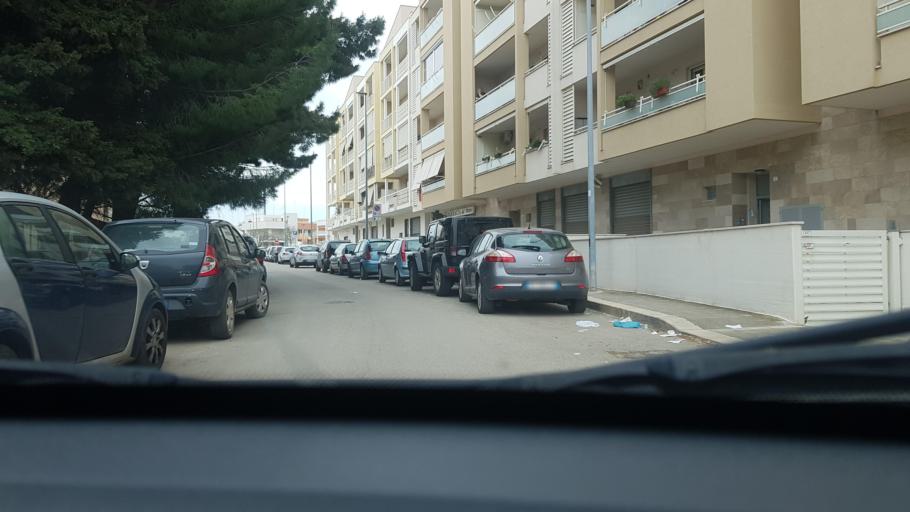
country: IT
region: Apulia
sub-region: Provincia di Bari
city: Noicattaro
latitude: 41.0392
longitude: 16.9852
